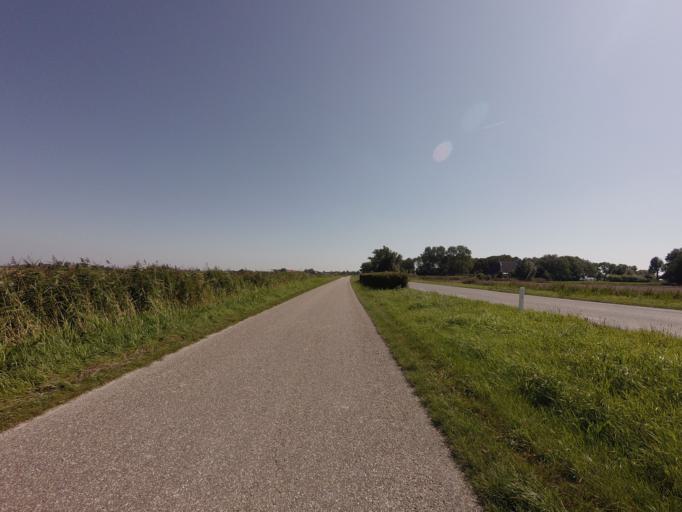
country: NL
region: Friesland
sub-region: Gemeente Dongeradeel
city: Ternaard
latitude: 53.3818
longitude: 6.0331
